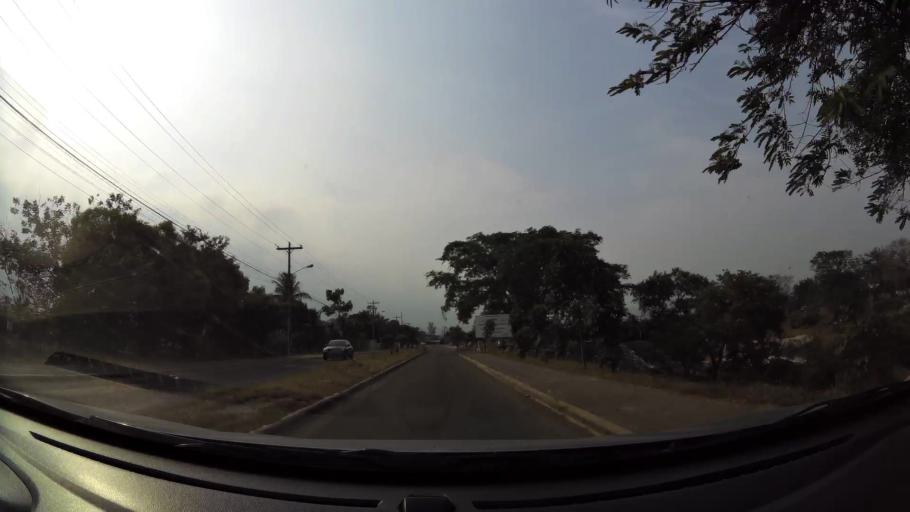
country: HN
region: Cortes
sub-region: San Pedro Sula
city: Pena Blanca
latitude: 15.5459
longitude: -88.0086
